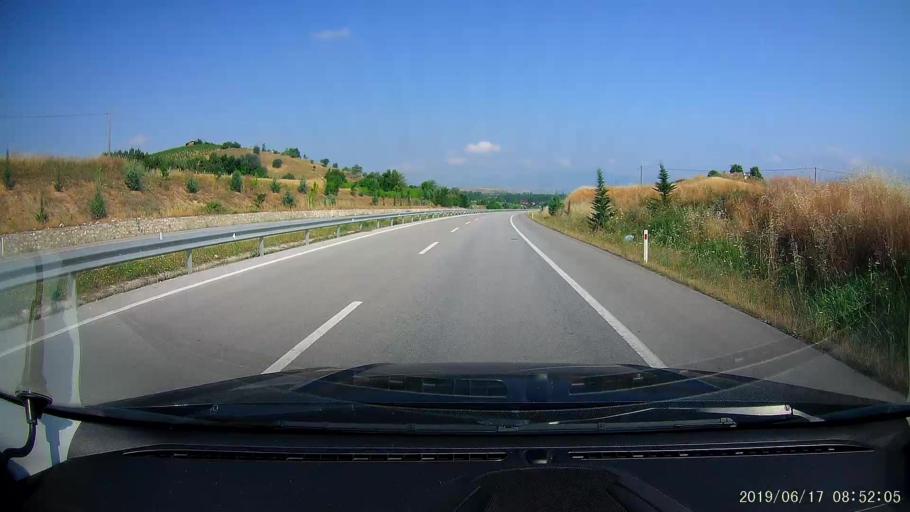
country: TR
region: Tokat
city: Erbaa
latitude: 40.6930
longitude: 36.5027
